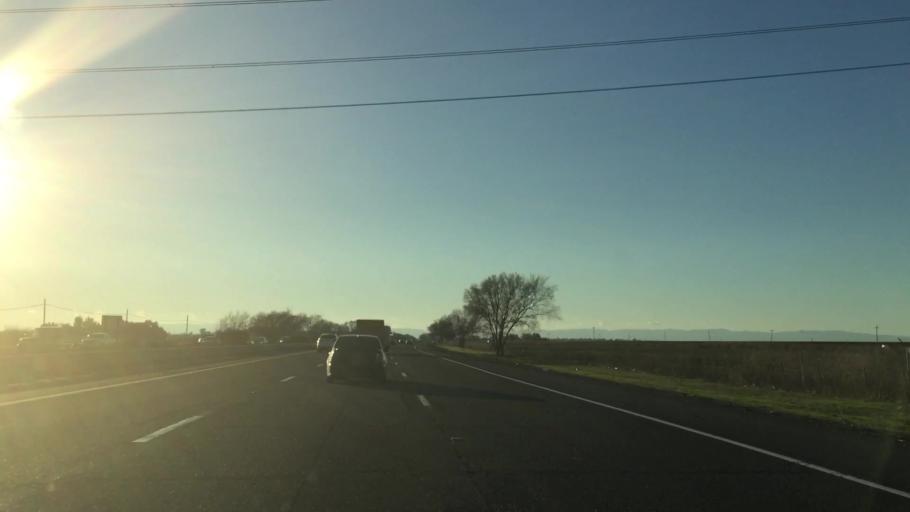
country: US
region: California
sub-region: Yolo County
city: Davis
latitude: 38.5614
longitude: -121.6519
